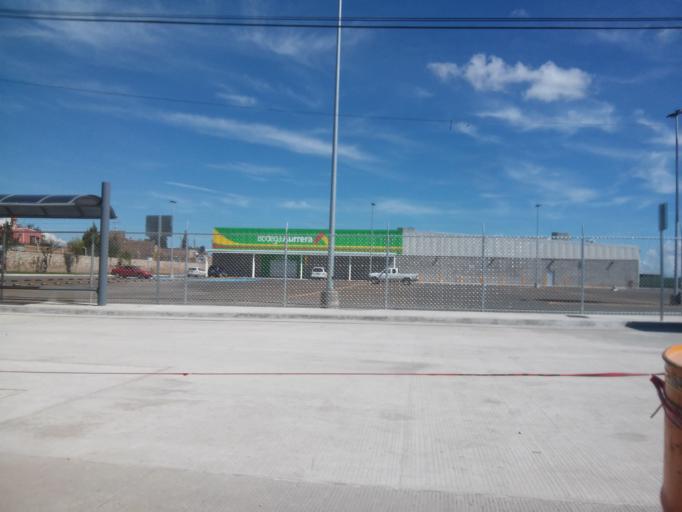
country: MX
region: Durango
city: Victoria de Durango
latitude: 23.9969
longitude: -104.6840
